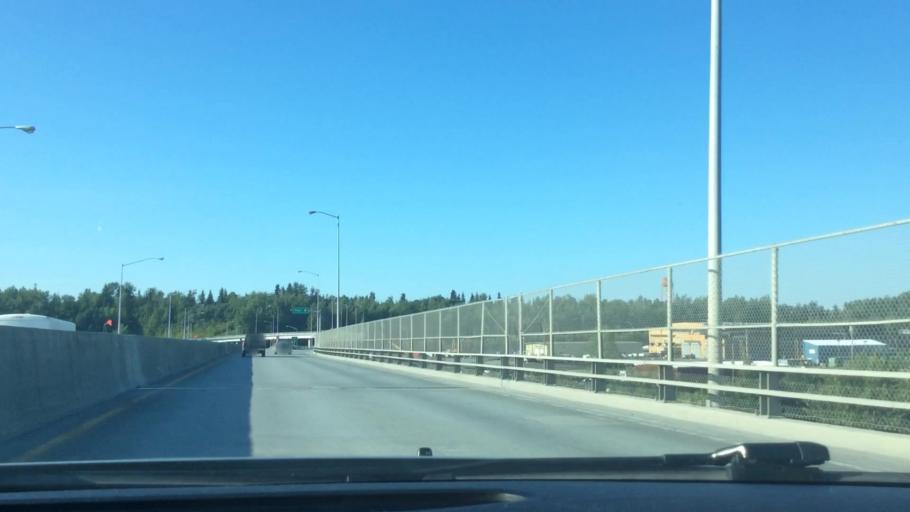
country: US
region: Alaska
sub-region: Anchorage Municipality
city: Anchorage
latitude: 61.2227
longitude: -149.8852
